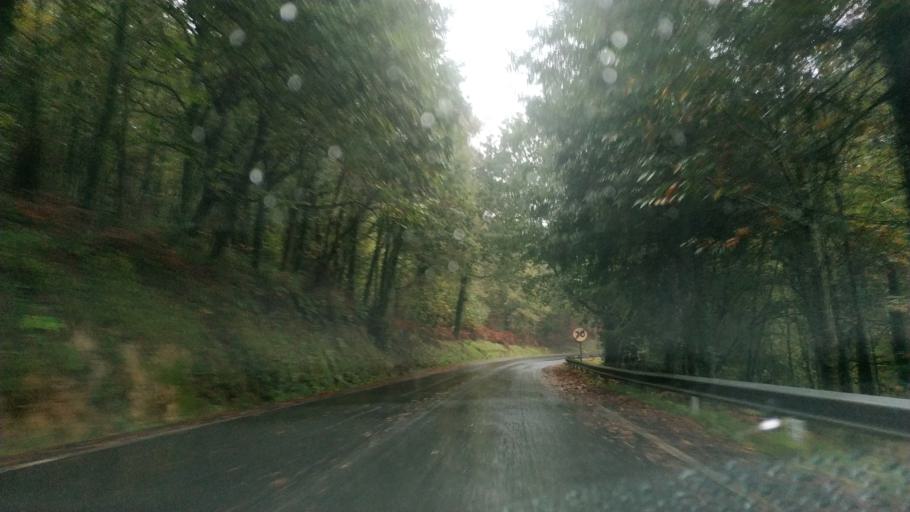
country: ES
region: Galicia
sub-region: Provincia da Coruna
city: Negreira
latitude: 42.9066
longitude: -8.7458
